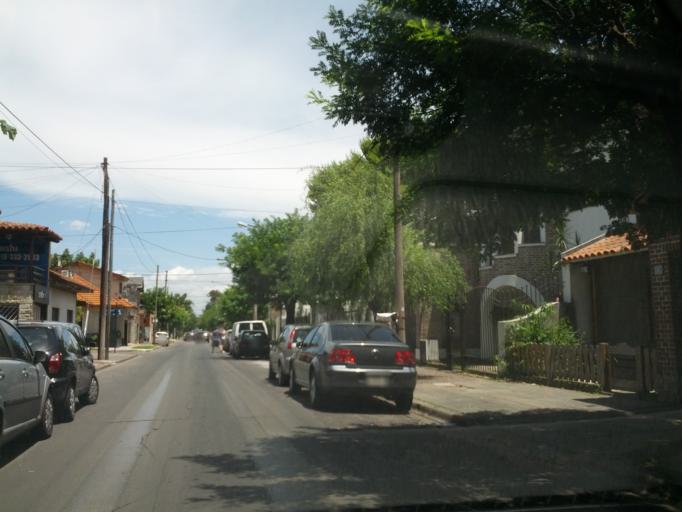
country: AR
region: Buenos Aires
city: San Justo
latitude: -34.6435
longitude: -58.5697
